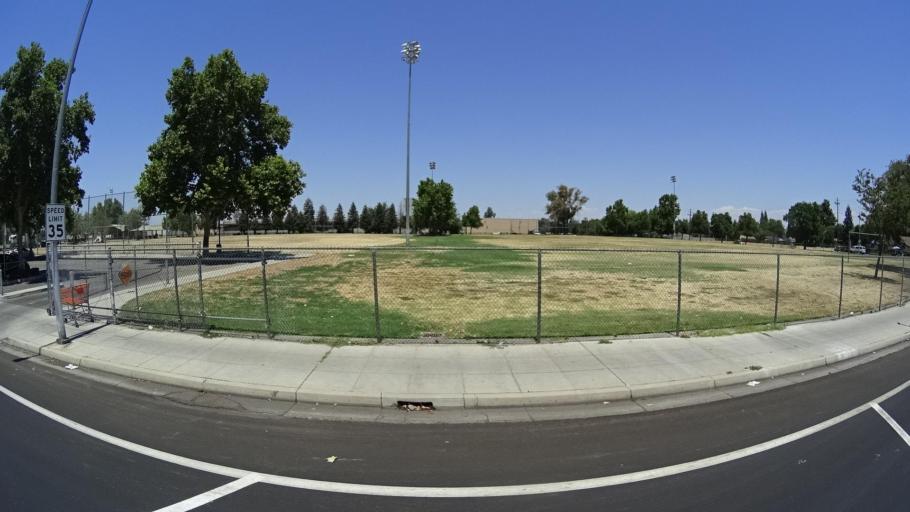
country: US
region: California
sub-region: Fresno County
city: Sunnyside
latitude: 36.7323
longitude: -119.7286
